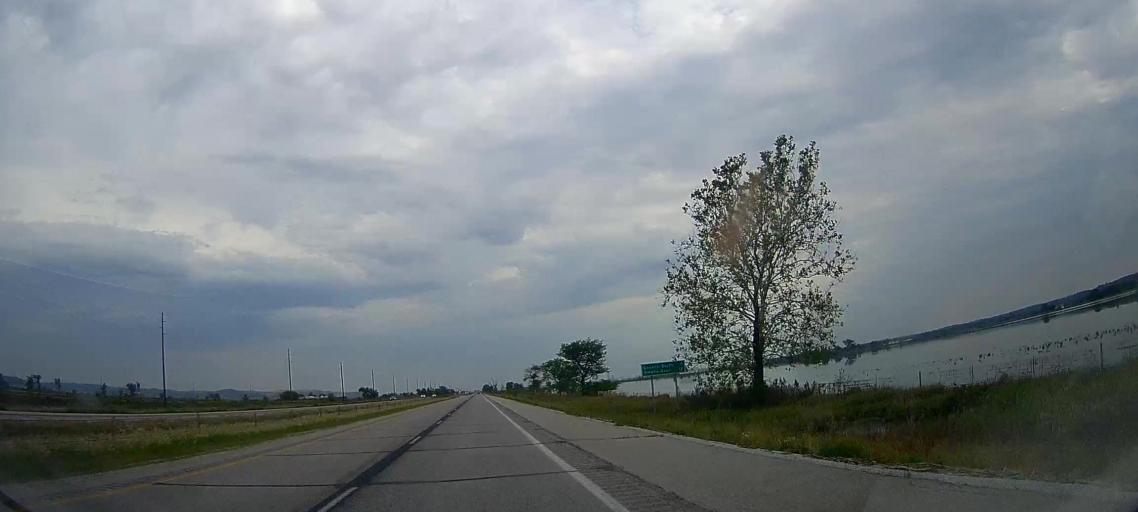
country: US
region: Iowa
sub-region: Pottawattamie County
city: Carter Lake
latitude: 41.4085
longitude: -95.8997
